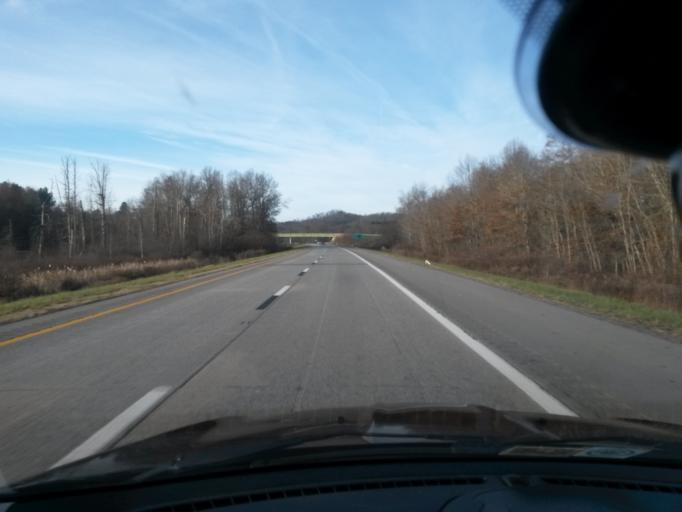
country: US
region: West Virginia
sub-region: Greenbrier County
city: Rainelle
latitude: 37.8999
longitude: -80.6469
